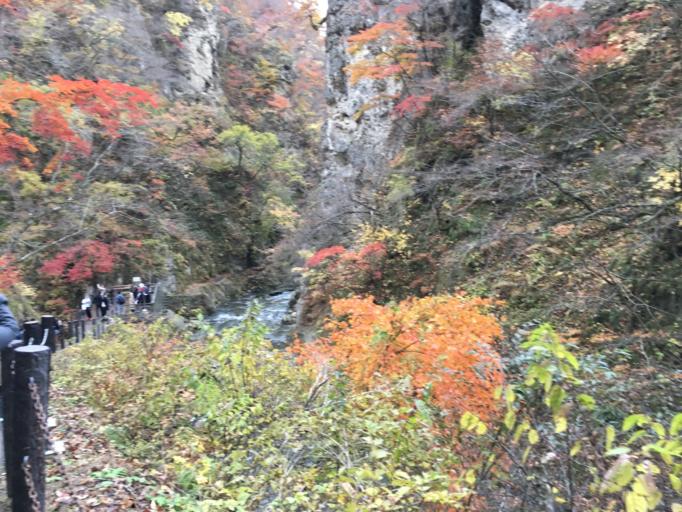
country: JP
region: Miyagi
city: Furukawa
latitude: 38.7298
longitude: 140.6899
